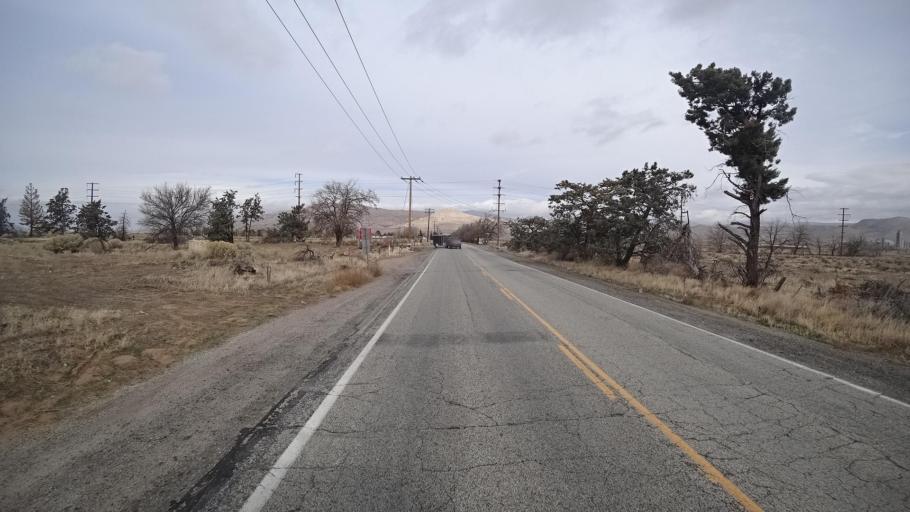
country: US
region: California
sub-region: Kern County
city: Tehachapi
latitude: 35.1089
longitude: -118.3967
